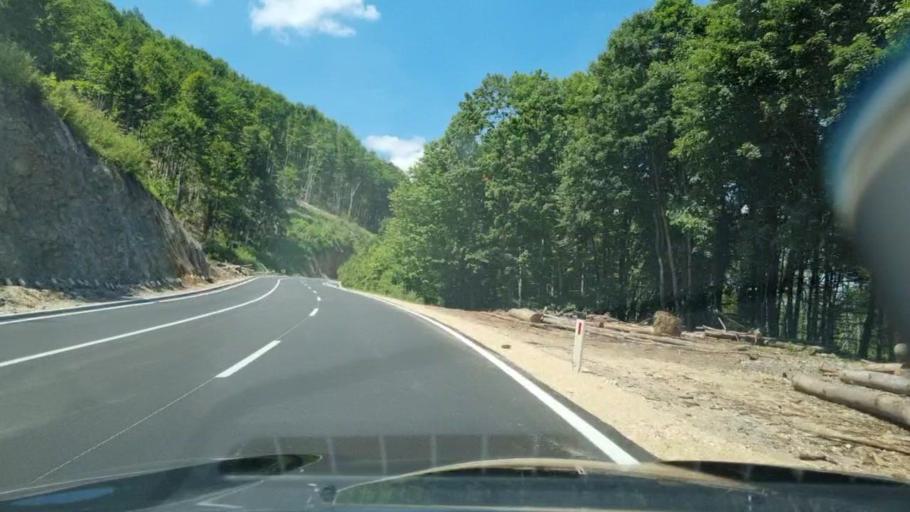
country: BA
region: Federation of Bosnia and Herzegovina
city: Velagici
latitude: 44.5459
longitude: 16.6881
